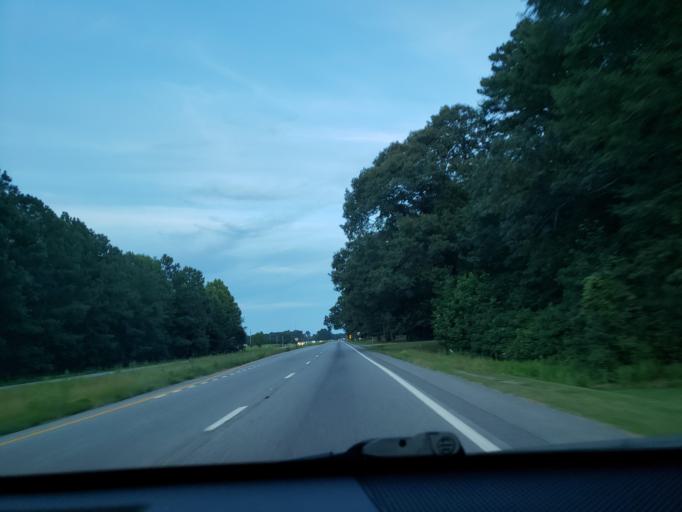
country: US
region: Virginia
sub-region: Southampton County
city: Courtland
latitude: 36.7074
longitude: -77.1517
